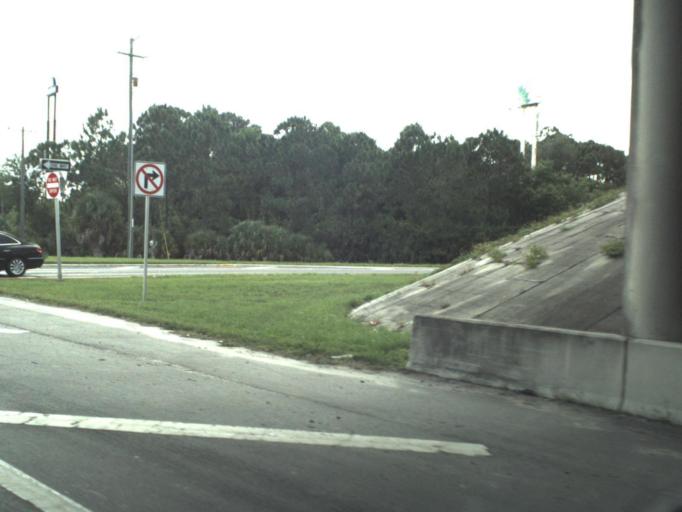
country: US
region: Florida
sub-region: Brevard County
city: Cocoa West
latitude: 28.3745
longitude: -80.8045
